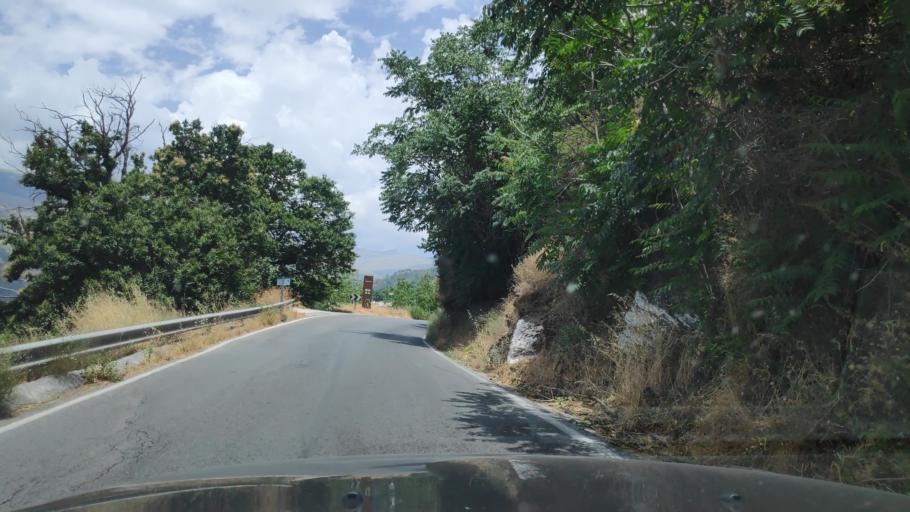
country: ES
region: Andalusia
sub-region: Provincia de Granada
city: Bubion
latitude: 36.9439
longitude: -3.3546
